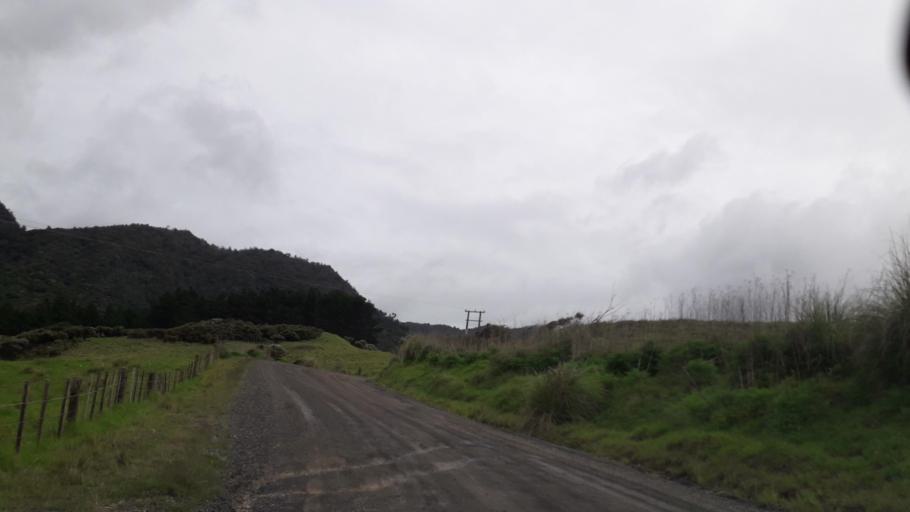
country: NZ
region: Northland
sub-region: Far North District
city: Kaitaia
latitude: -35.4136
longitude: 173.3663
